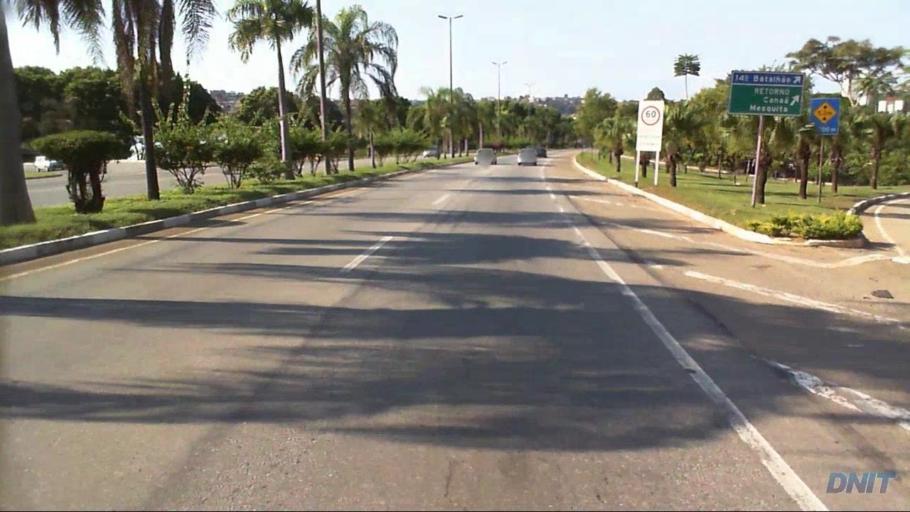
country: BR
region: Minas Gerais
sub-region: Ipatinga
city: Ipatinga
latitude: -19.4733
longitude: -42.5412
